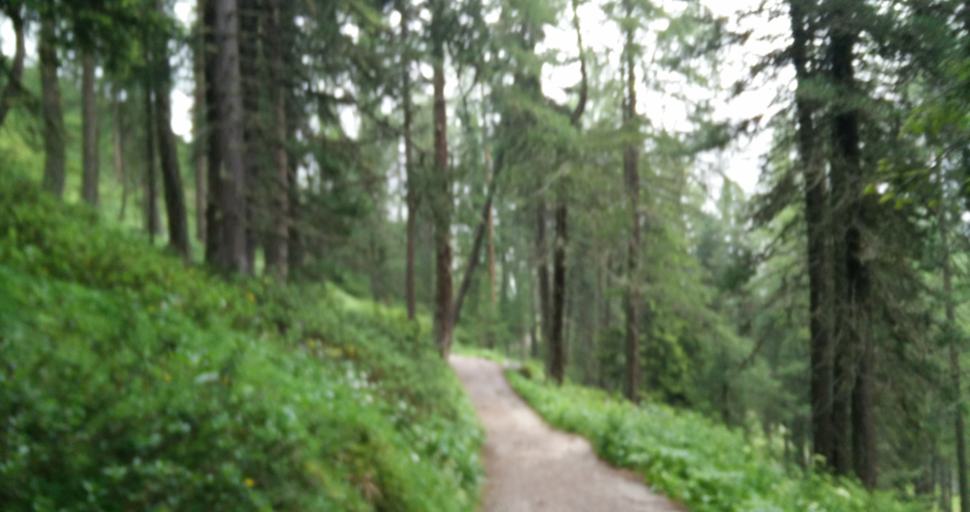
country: IT
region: Trentino-Alto Adige
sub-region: Provincia di Trento
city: Vigo di Fassa
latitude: 46.4350
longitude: 11.6581
